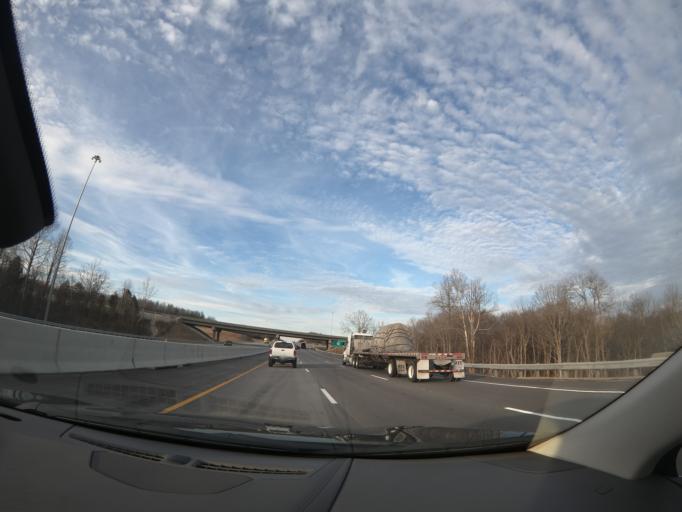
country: US
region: Kentucky
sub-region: Hart County
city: Munfordville
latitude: 37.3778
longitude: -85.8889
